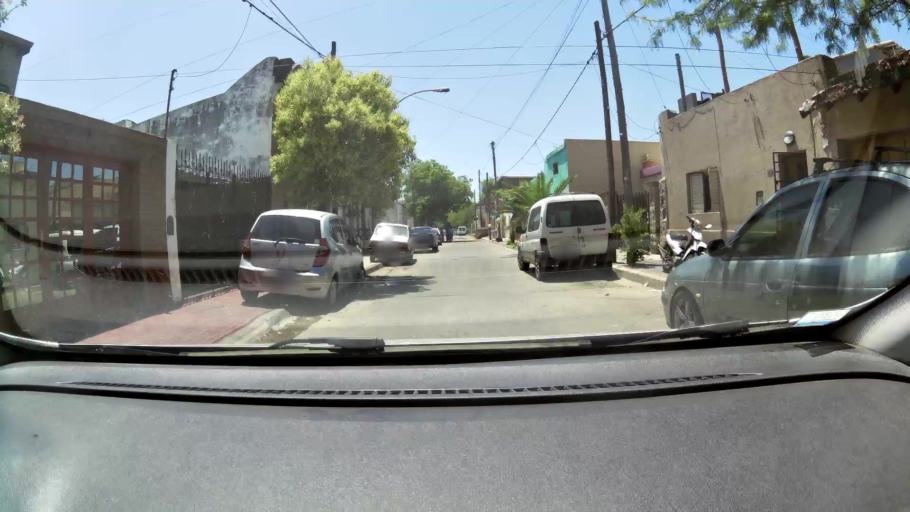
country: AR
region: Cordoba
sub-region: Departamento de Capital
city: Cordoba
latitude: -31.4041
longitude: -64.2037
